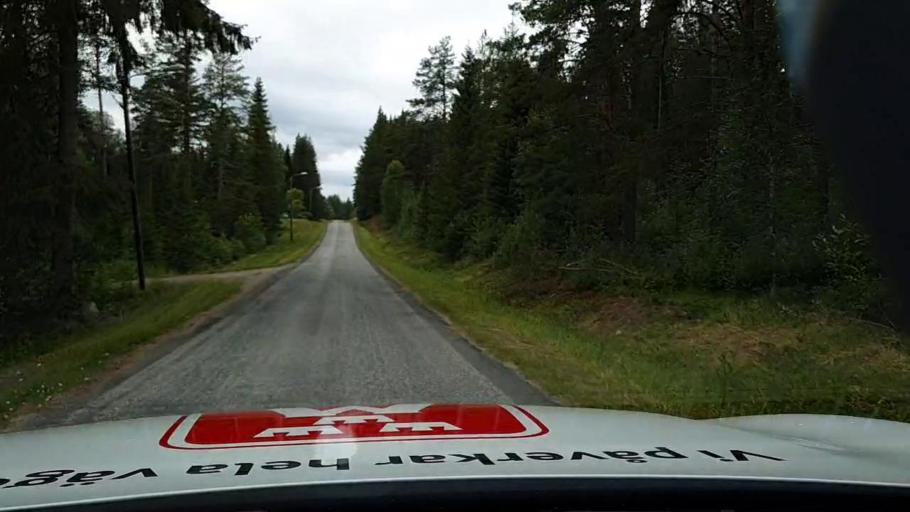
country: SE
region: Vaesterbotten
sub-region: Dorotea Kommun
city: Dorotea
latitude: 64.1000
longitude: 16.4051
